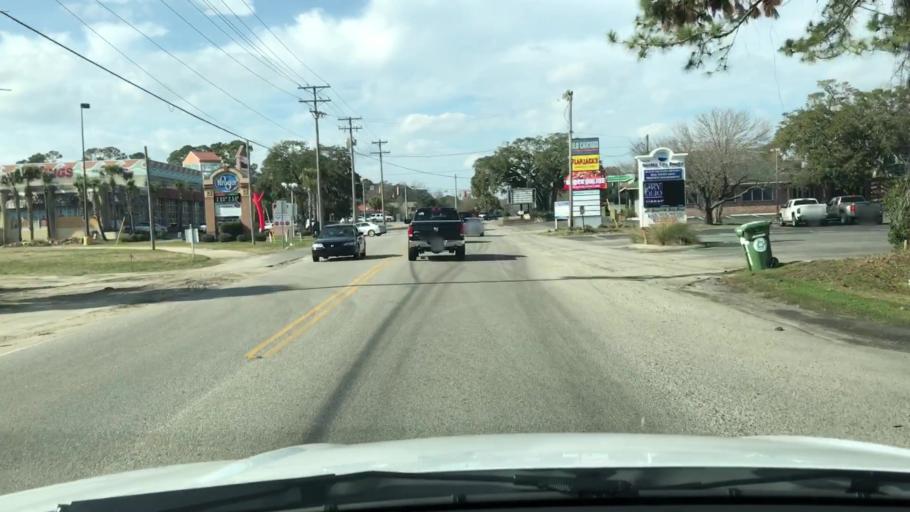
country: US
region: South Carolina
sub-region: Horry County
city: Garden City
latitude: 33.5850
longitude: -79.0109
